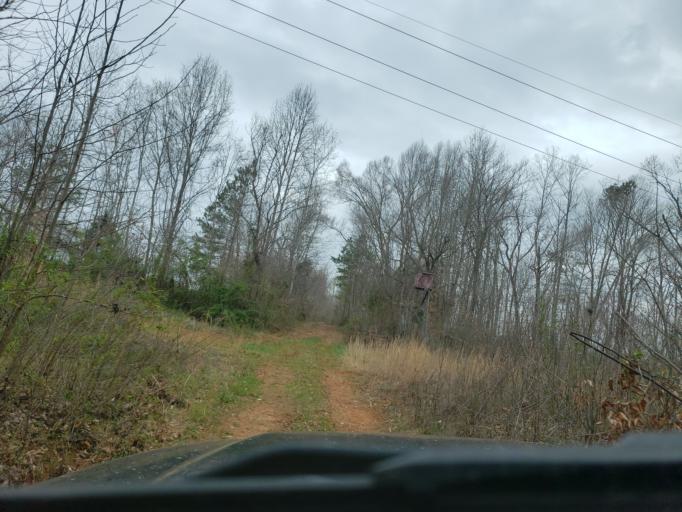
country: US
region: North Carolina
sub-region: Cleveland County
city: White Plains
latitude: 35.1883
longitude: -81.3697
